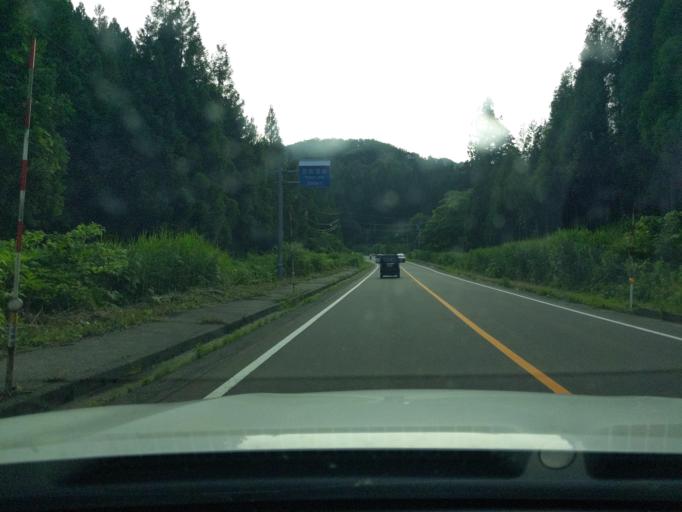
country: JP
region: Niigata
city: Kashiwazaki
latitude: 37.4121
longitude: 138.6770
